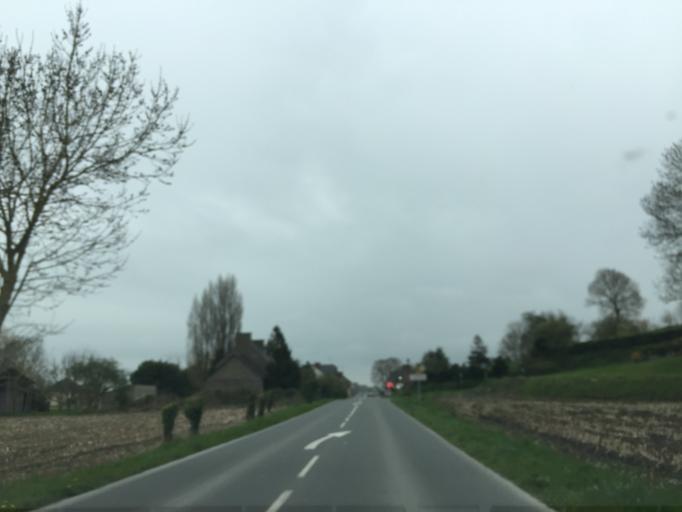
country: FR
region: Brittany
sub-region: Departement d'Ille-et-Vilaine
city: Pleine-Fougeres
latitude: 48.5705
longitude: -1.5483
